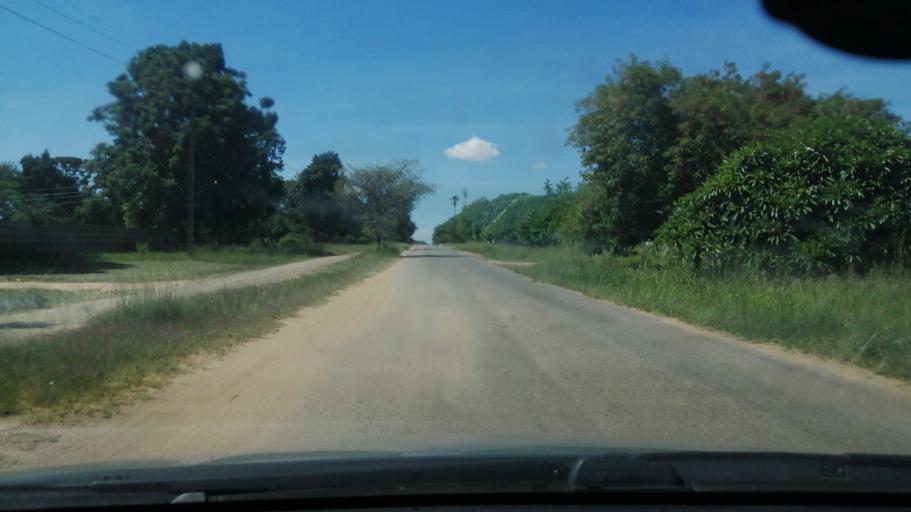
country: ZW
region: Harare
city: Epworth
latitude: -17.8229
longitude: 31.1262
